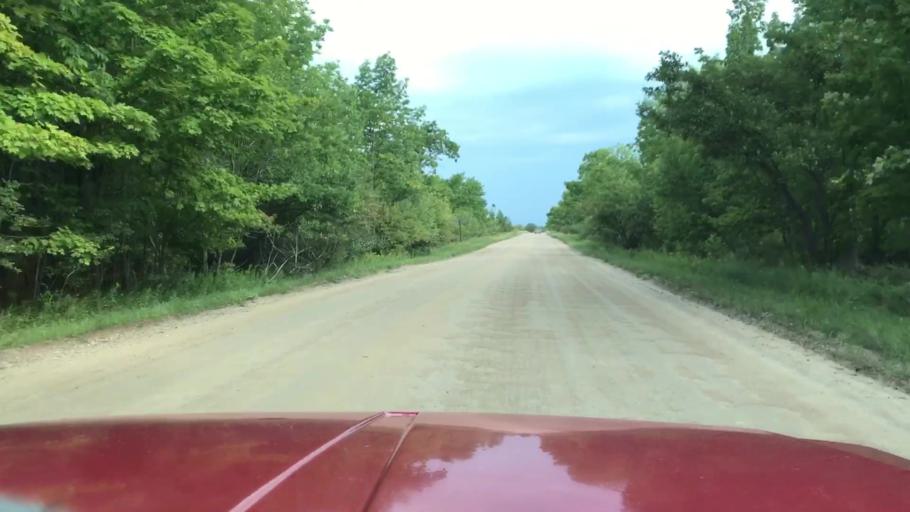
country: US
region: Michigan
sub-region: Charlevoix County
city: Charlevoix
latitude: 45.7218
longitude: -85.5158
